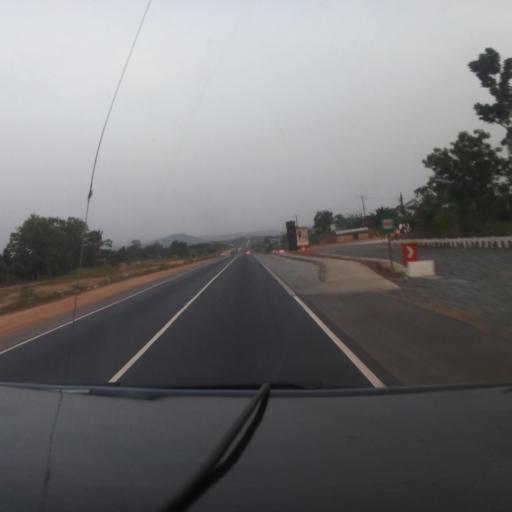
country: GH
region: Eastern
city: Nsawam
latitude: 5.8756
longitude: -0.3711
